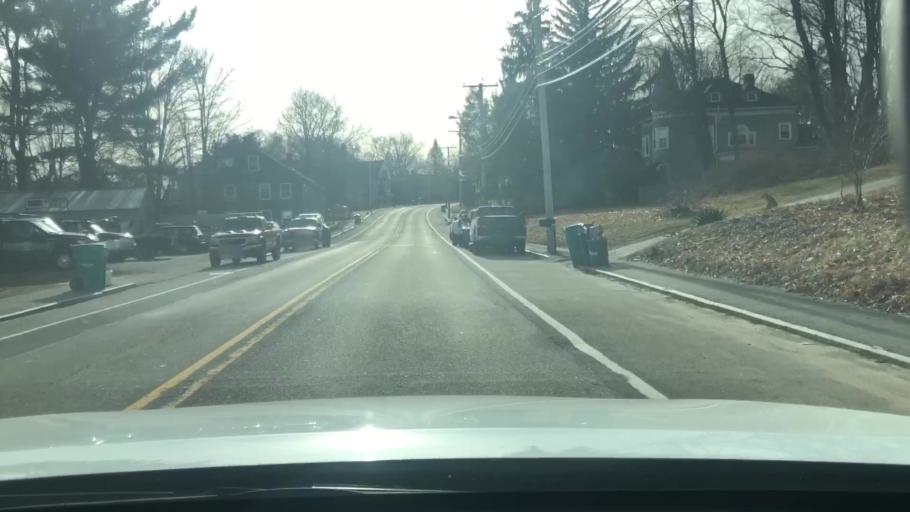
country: US
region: Massachusetts
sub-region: Worcester County
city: Upton
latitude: 42.1723
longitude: -71.6040
